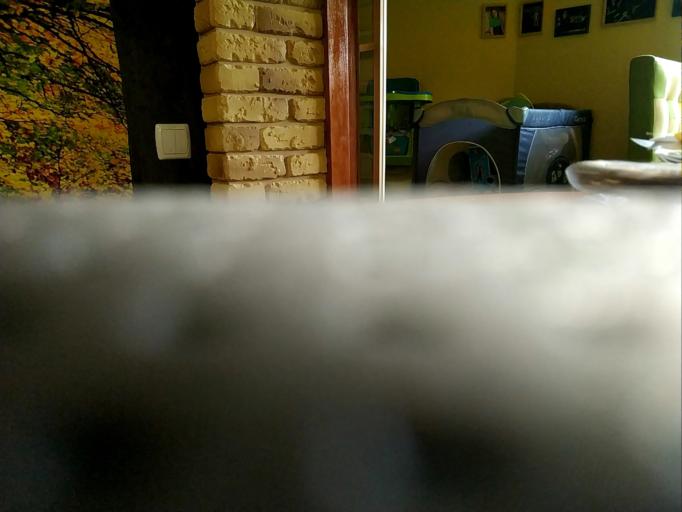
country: RU
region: Kaluga
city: Seredeyskiy
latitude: 53.9085
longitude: 35.3522
